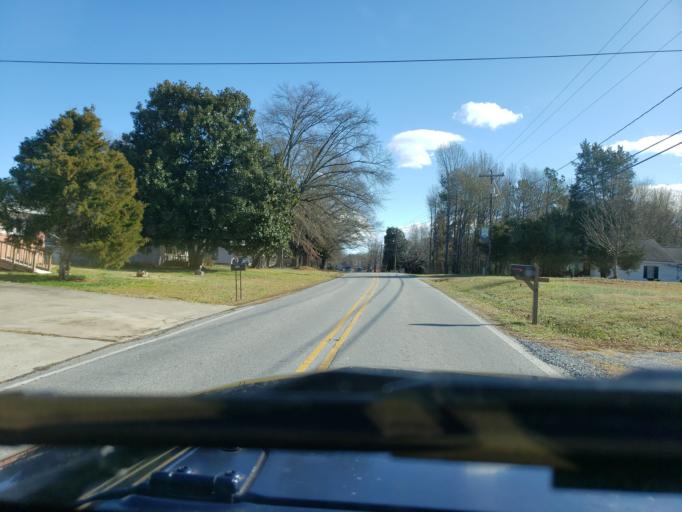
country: US
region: North Carolina
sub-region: Cleveland County
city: White Plains
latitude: 35.1806
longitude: -81.4594
